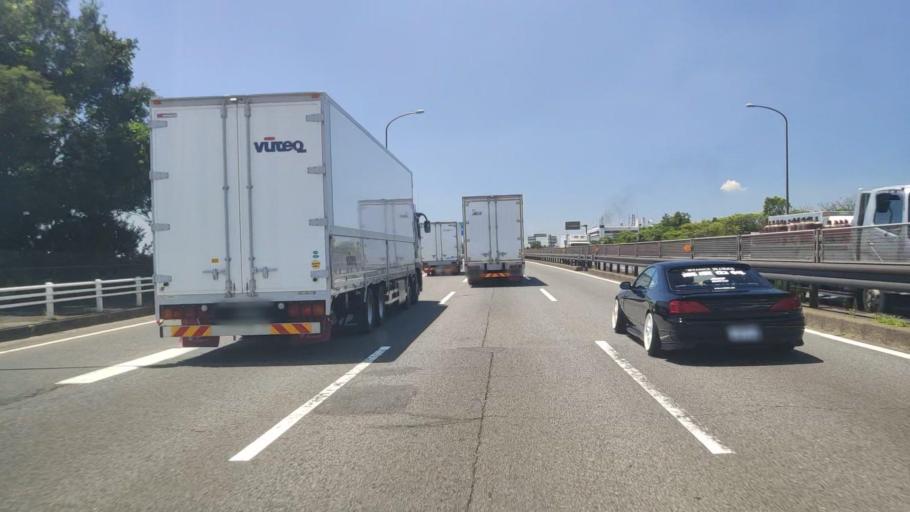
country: JP
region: Aichi
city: Kanie
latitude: 35.0830
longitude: 136.8271
